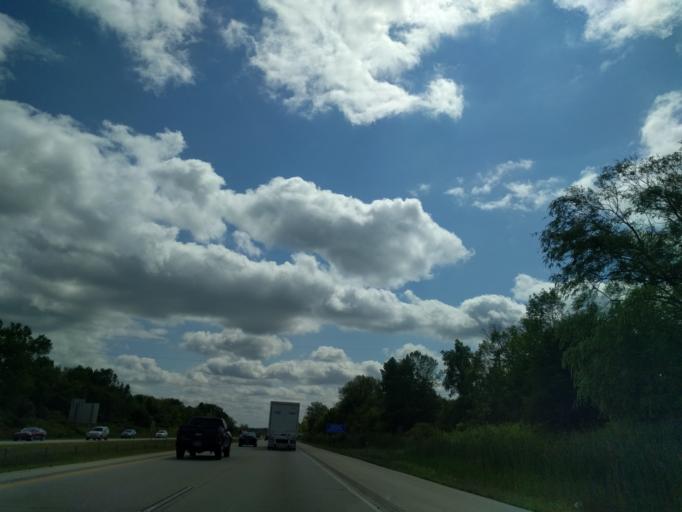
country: US
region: Wisconsin
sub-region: Milwaukee County
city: River Hills
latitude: 43.2044
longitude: -87.9222
